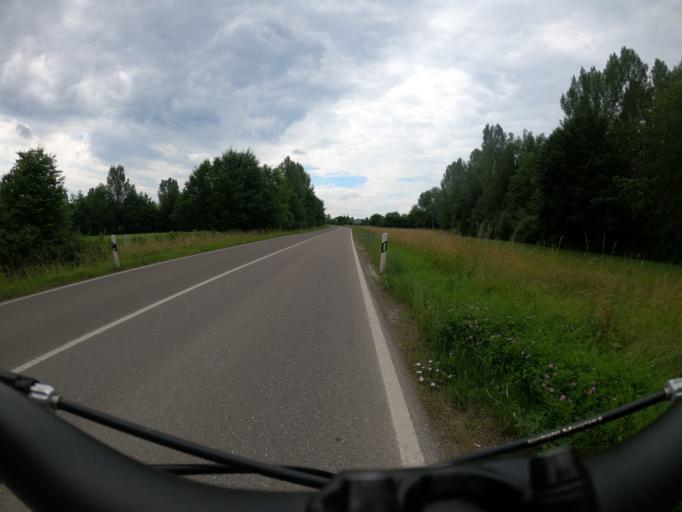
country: DE
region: Bavaria
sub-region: Swabia
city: Neu-Ulm
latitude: 48.4148
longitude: 10.0232
